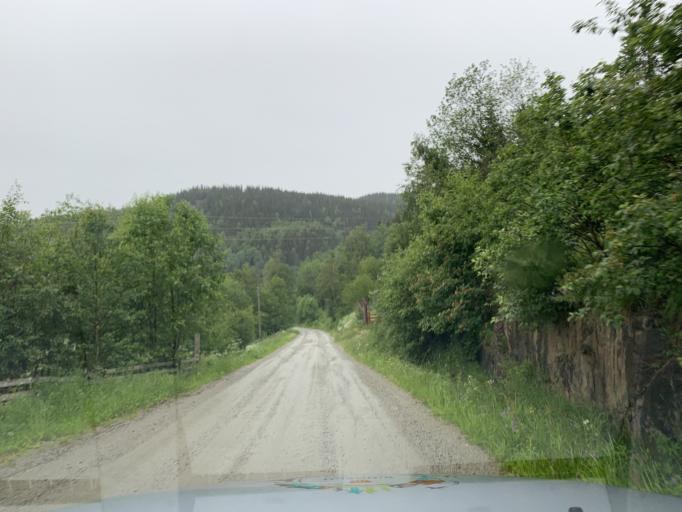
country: NO
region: Oppland
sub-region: Oyer
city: Tretten
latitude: 61.3895
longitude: 10.2788
